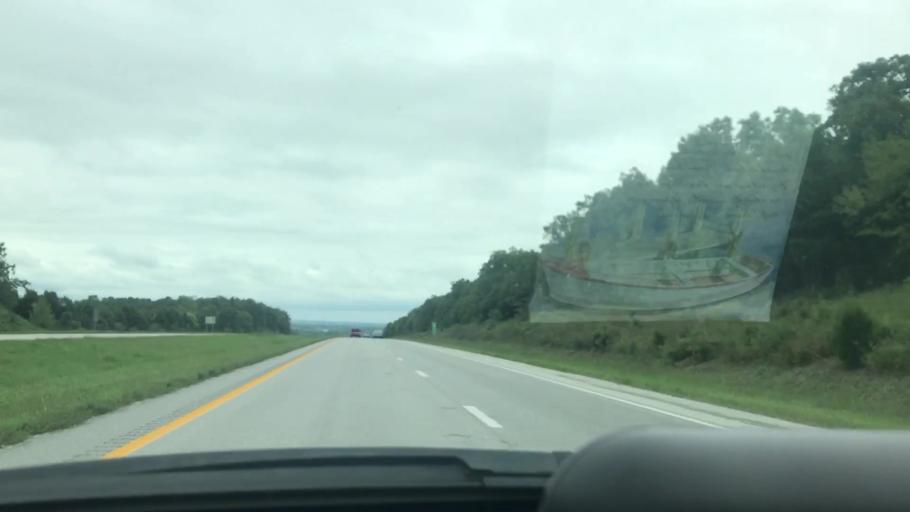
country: US
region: Missouri
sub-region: Greene County
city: Fair Grove
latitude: 37.3305
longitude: -93.1680
